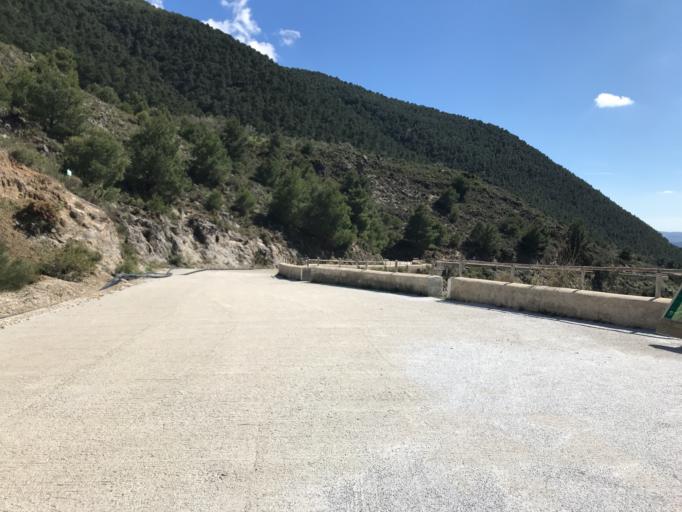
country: ES
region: Andalusia
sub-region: Provincia de Malaga
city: Alcaucin
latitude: 36.9172
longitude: -4.1012
